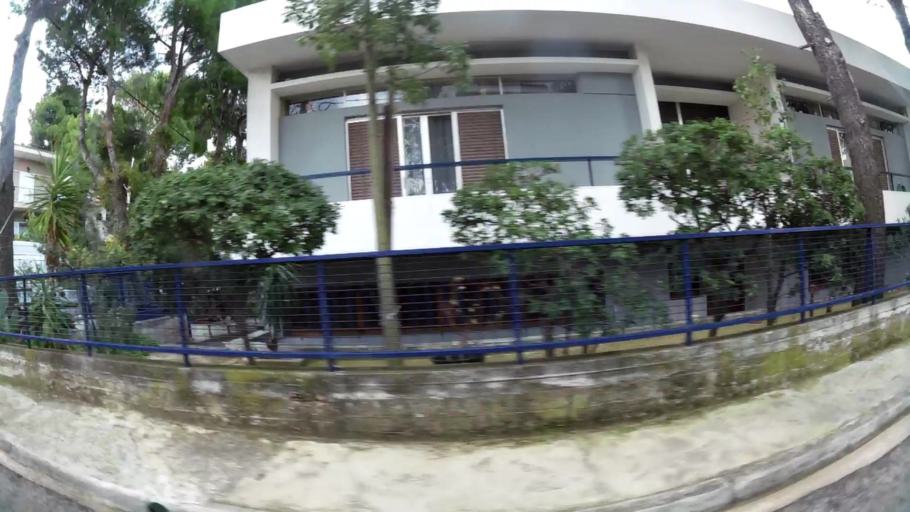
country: GR
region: Attica
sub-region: Nomarchia Athinas
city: Melissia
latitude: 38.0440
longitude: 23.8348
